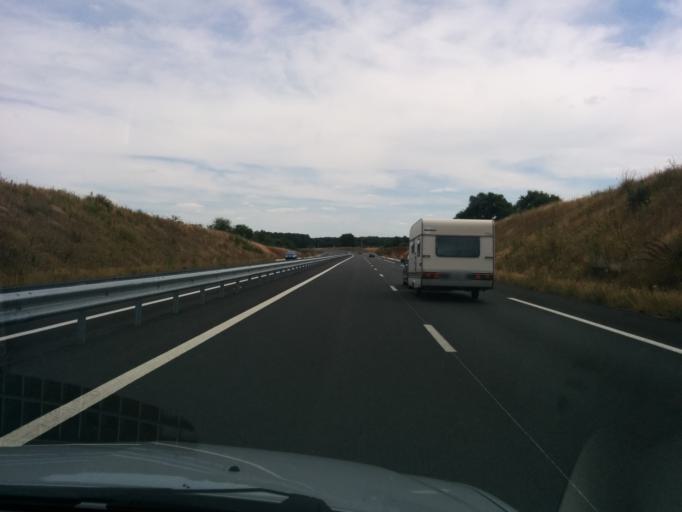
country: FR
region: Poitou-Charentes
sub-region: Departement des Deux-Sevres
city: Nueil-les-Aubiers
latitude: 46.8599
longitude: -0.5675
